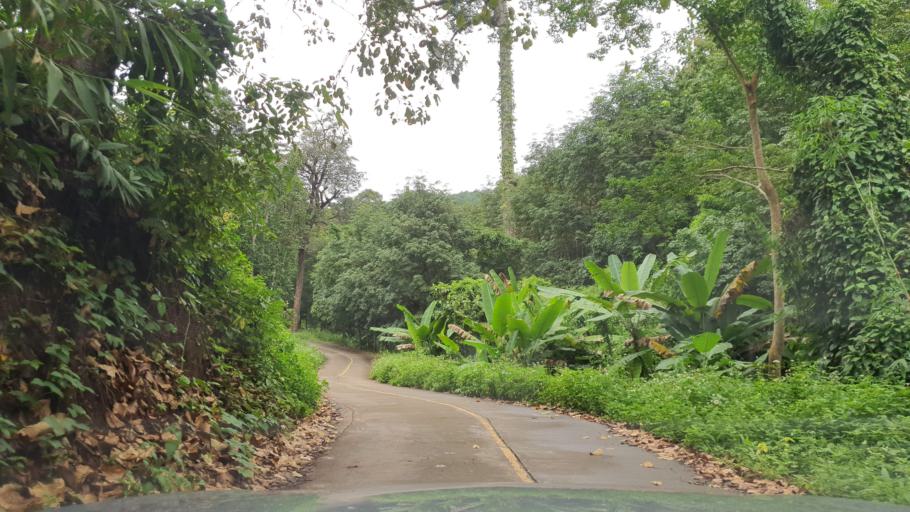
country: TH
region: Chiang Mai
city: Mae Taeng
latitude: 19.2229
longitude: 98.9245
